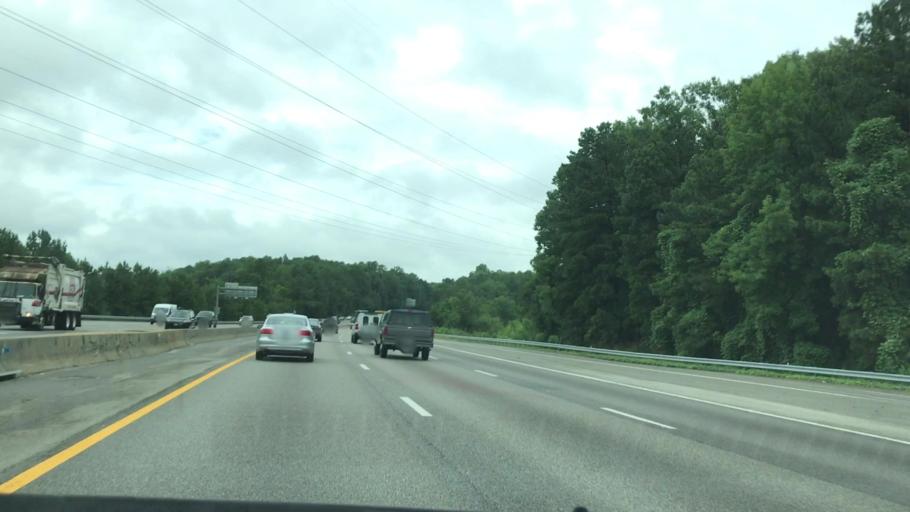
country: US
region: Virginia
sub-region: City of Colonial Heights
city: Colonial Heights
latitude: 37.3141
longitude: -77.3995
